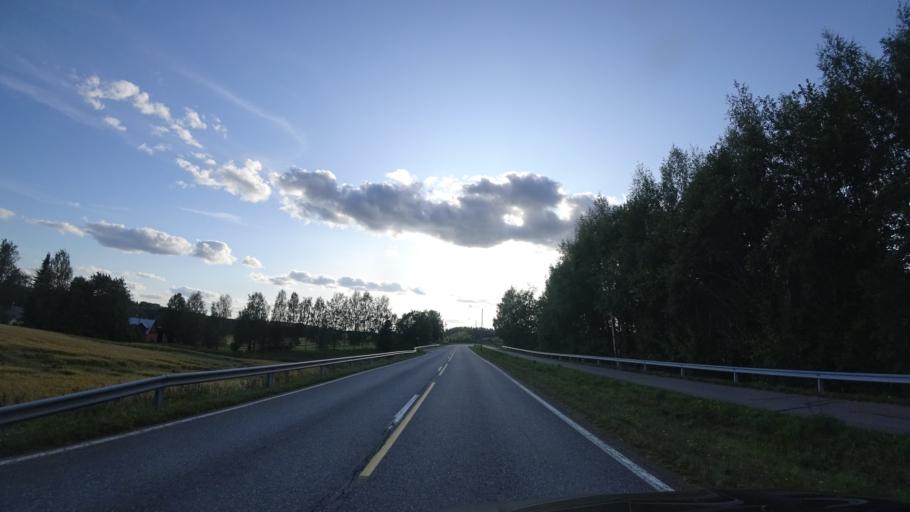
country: FI
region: Haeme
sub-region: Haemeenlinna
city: Lammi
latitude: 61.0810
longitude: 25.0452
